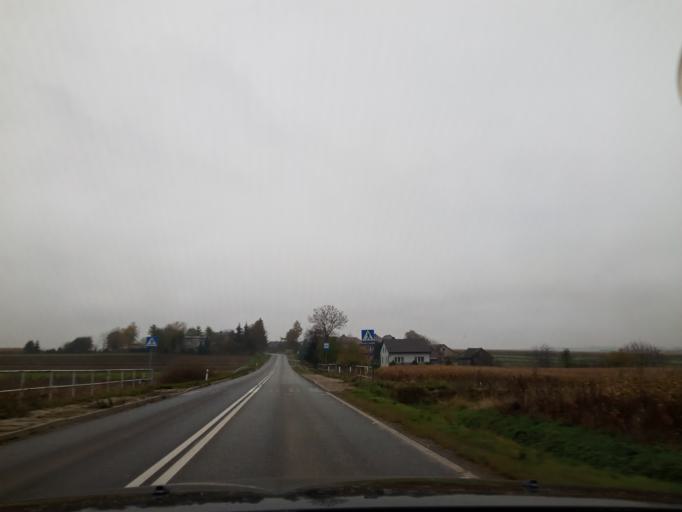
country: PL
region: Lesser Poland Voivodeship
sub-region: Powiat proszowicki
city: Klimontow
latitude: 50.2127
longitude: 20.3116
